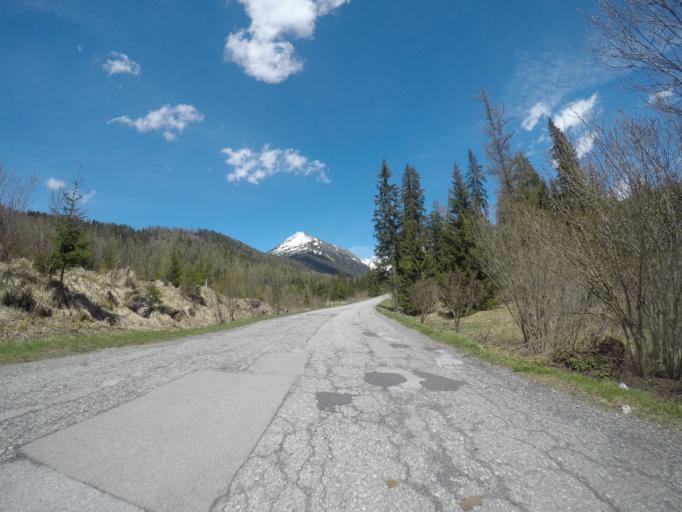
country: SK
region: Presovsky
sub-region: Okres Poprad
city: Strba
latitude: 49.1210
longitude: 20.0749
